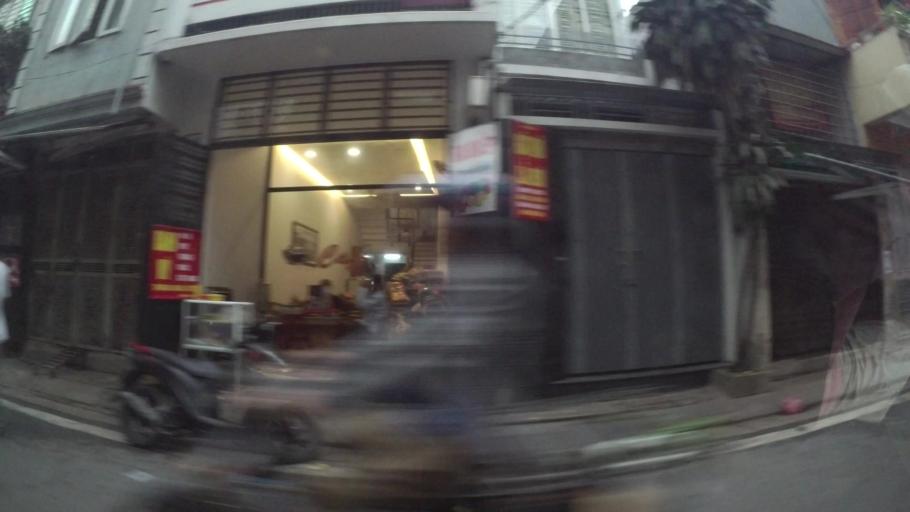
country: VN
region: Ha Noi
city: Hai BaTrung
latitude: 21.0109
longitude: 105.8673
